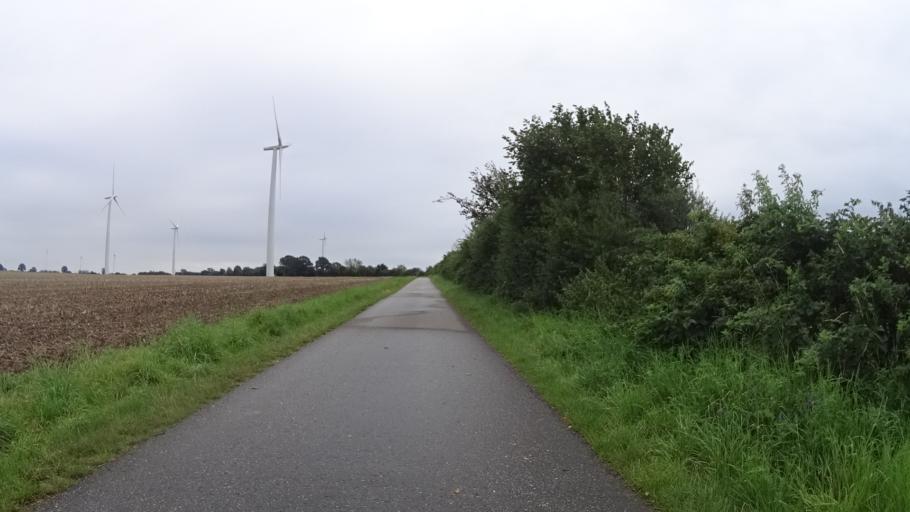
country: DE
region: Schleswig-Holstein
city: Stubben
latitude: 53.7159
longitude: 10.4234
